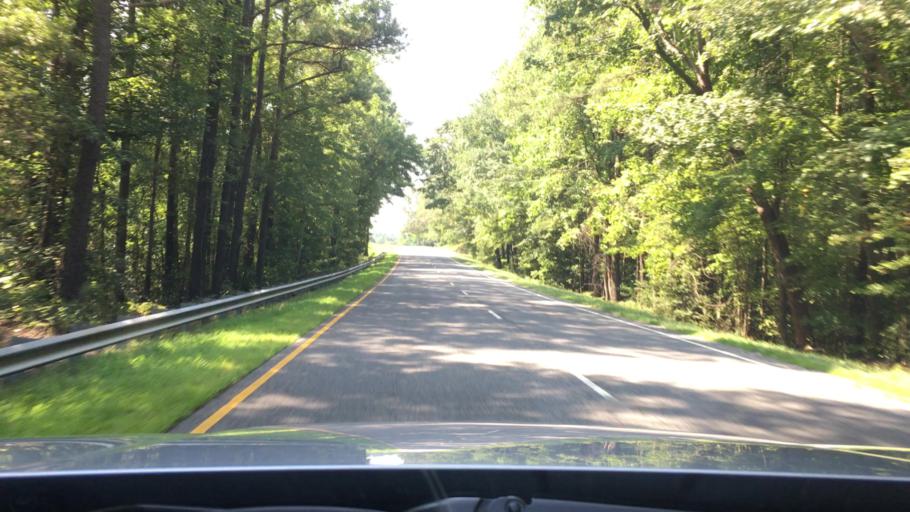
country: US
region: Virginia
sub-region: Caroline County
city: Bowling Green
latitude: 37.9957
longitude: -77.4170
